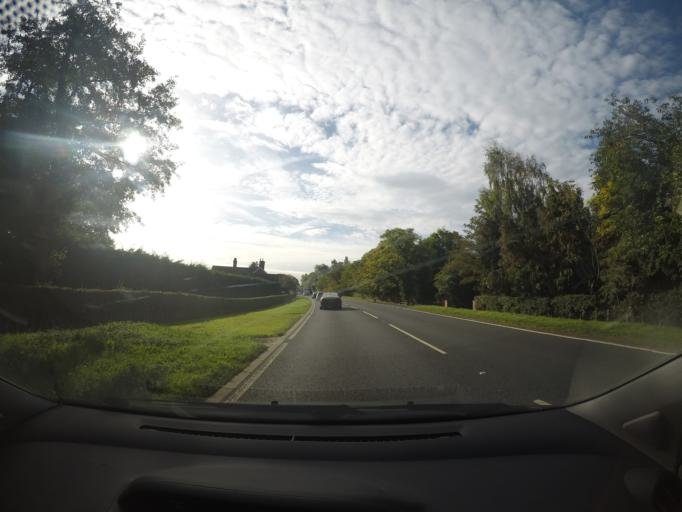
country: GB
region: England
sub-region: City of York
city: Deighton
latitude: 53.9047
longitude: -1.0499
